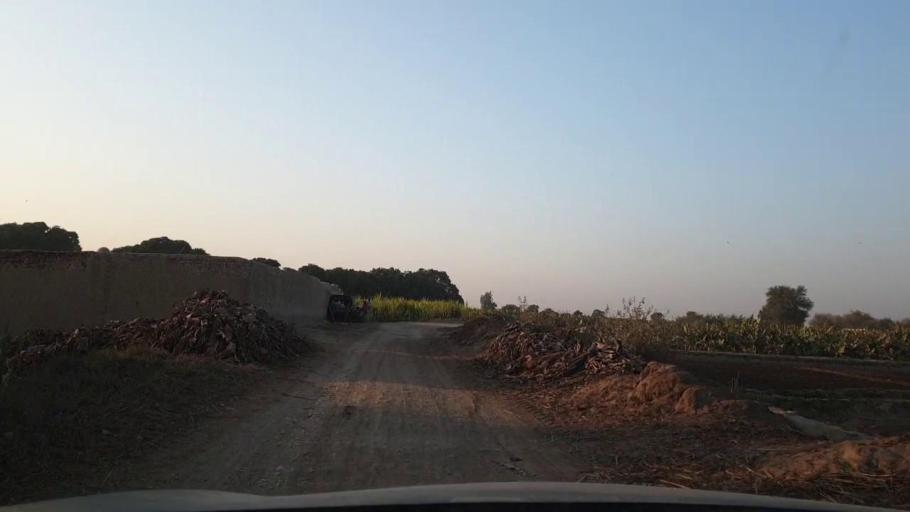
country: PK
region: Sindh
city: Tando Allahyar
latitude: 25.4961
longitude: 68.7411
